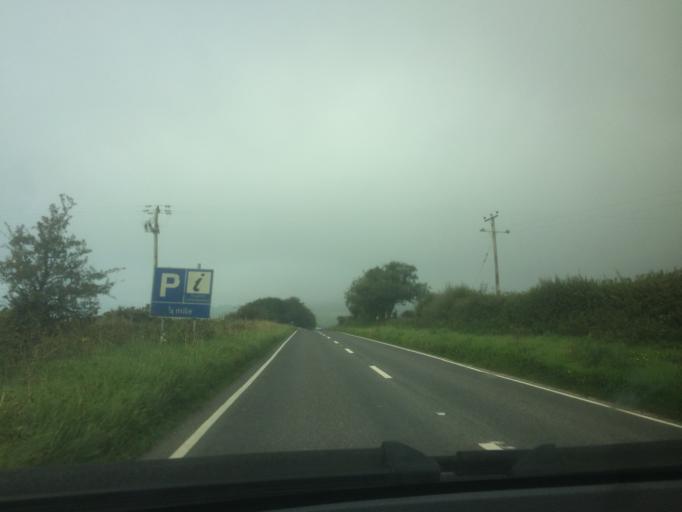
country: GB
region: England
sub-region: Cornwall
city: Gunnislake
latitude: 50.5164
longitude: -4.2597
